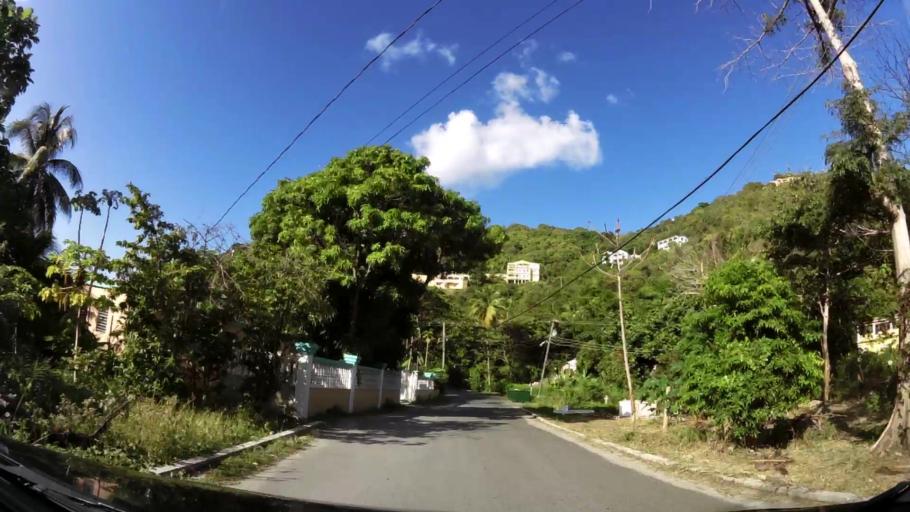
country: VG
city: Road Town
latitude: 18.4137
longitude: -64.6704
